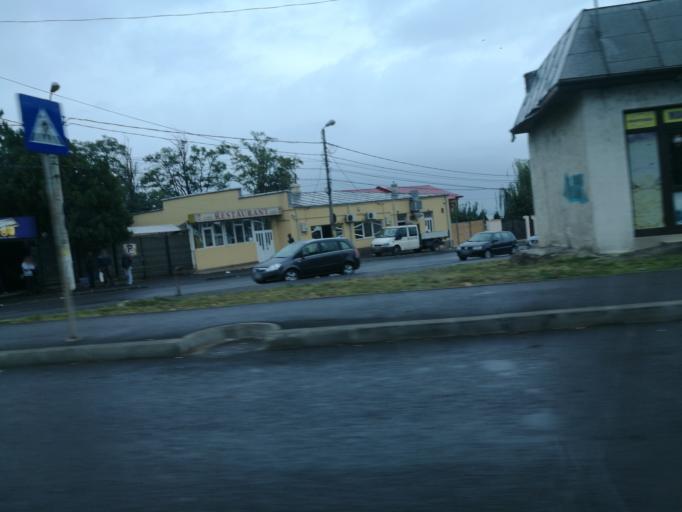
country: RO
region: Galati
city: Galati
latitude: 45.4657
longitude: 28.0356
